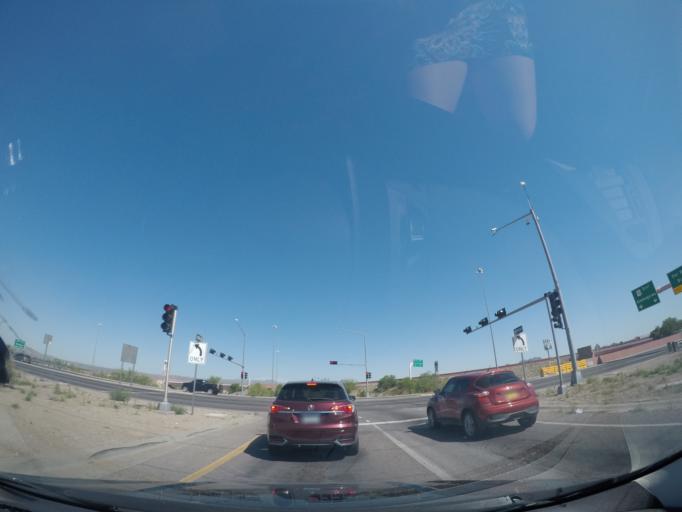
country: US
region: New Mexico
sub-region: Dona Ana County
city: Las Cruces
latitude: 32.3487
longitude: -106.7685
